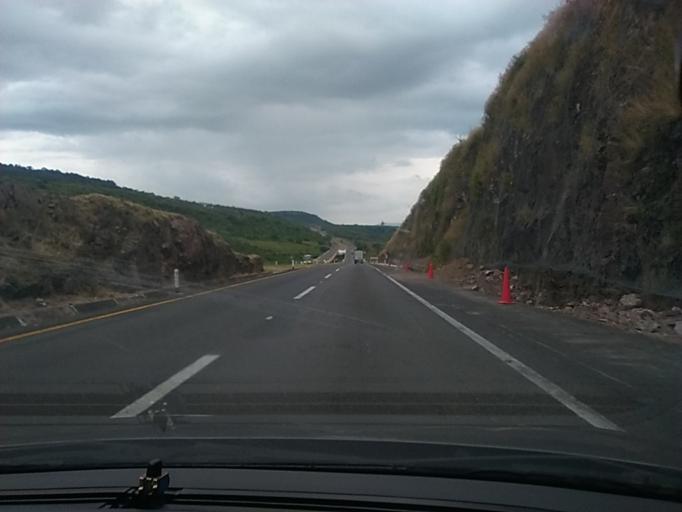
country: MX
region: Jalisco
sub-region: Zapotlan del Rey
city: Zapotlan del Rey
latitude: 20.4957
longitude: -102.9459
